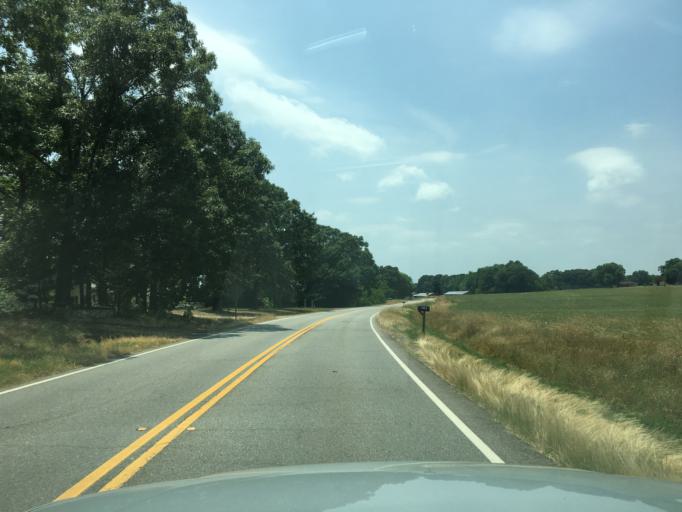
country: US
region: Georgia
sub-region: Madison County
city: Danielsville
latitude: 34.2160
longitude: -83.2294
